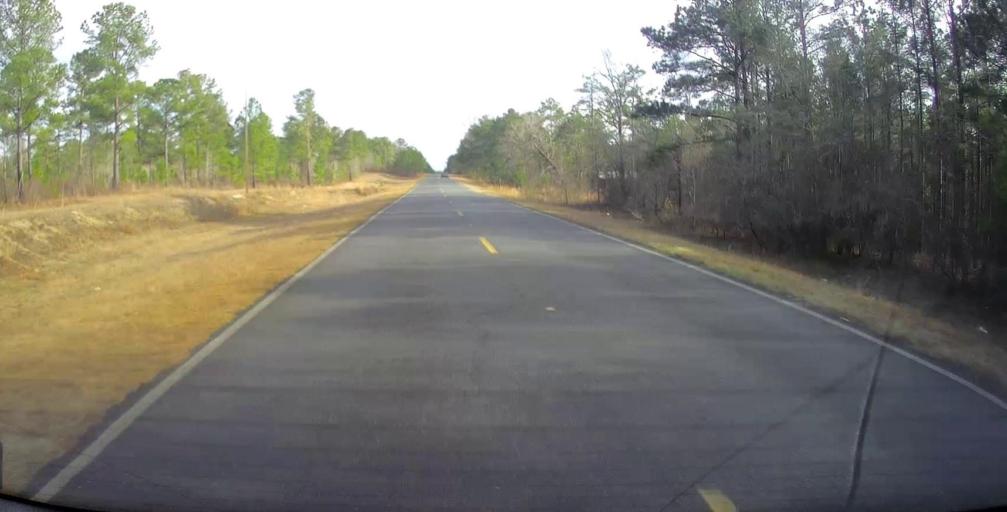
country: US
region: Georgia
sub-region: Talbot County
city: Talbotton
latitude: 32.5085
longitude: -84.5890
